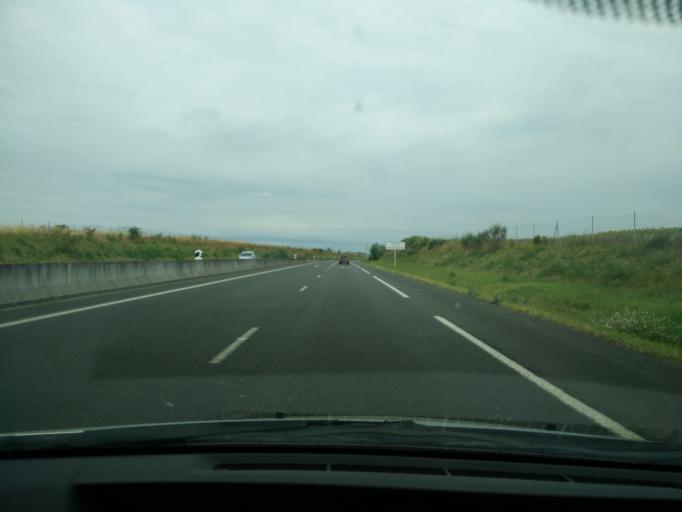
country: FR
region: Pays de la Loire
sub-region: Departement de Maine-et-Loire
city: Saint-Jean
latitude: 47.2514
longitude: -0.3291
